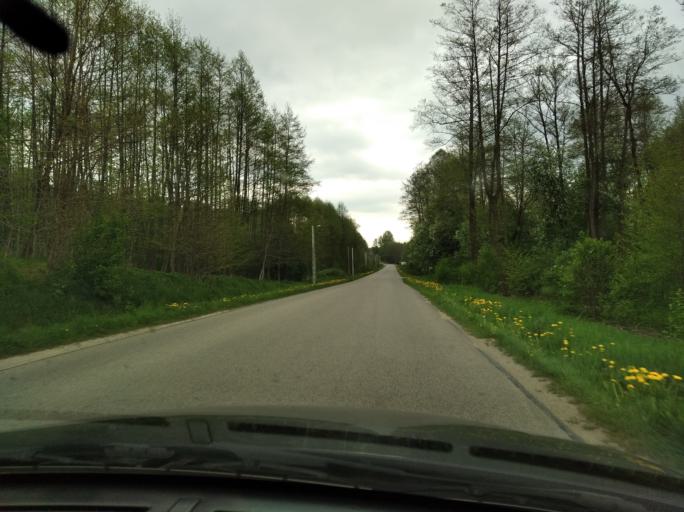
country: PL
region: Subcarpathian Voivodeship
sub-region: Powiat debicki
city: Leki Gorne
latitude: 49.9754
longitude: 21.1678
